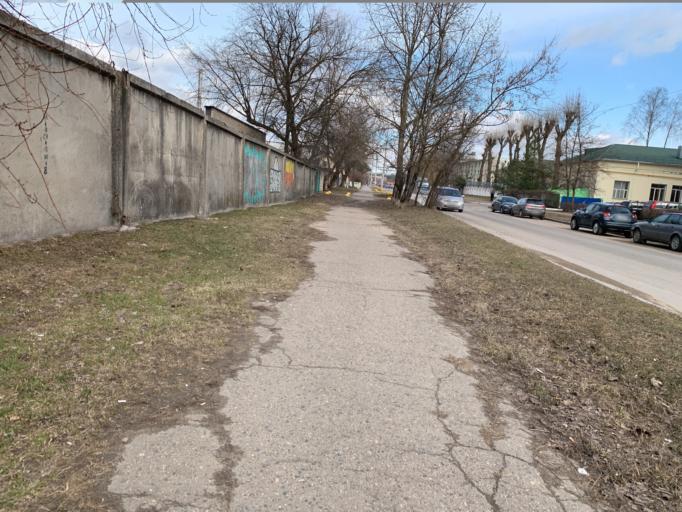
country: BY
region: Minsk
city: Minsk
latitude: 53.9064
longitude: 27.5996
